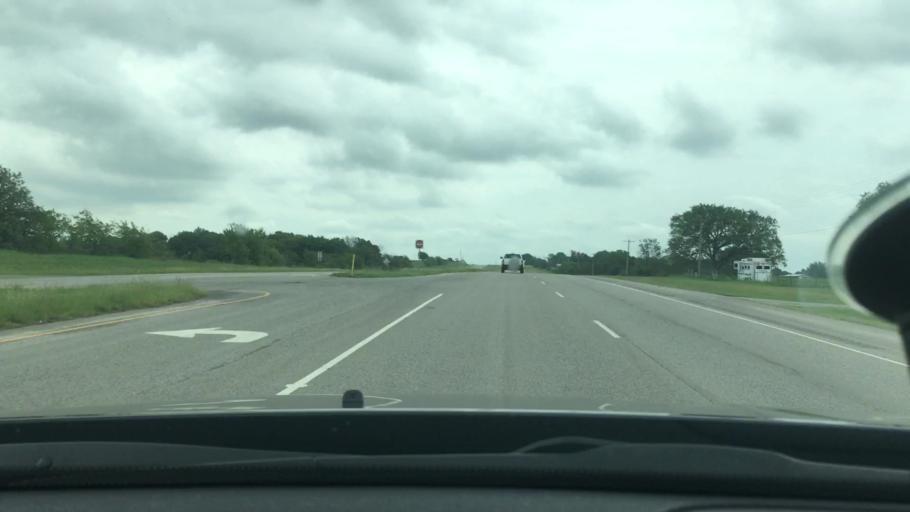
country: US
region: Oklahoma
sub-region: Carter County
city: Wilson
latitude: 34.1729
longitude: -97.4722
